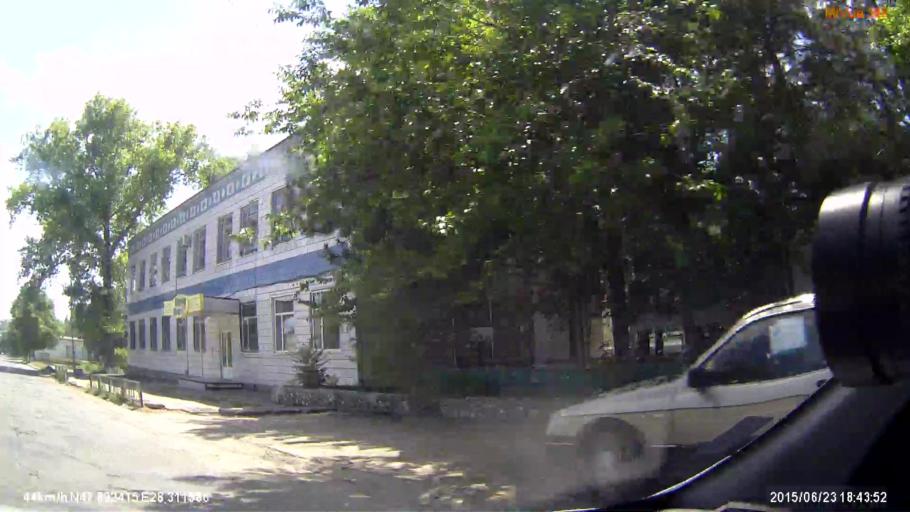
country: MD
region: Floresti
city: Floresti
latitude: 47.8926
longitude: 28.3116
